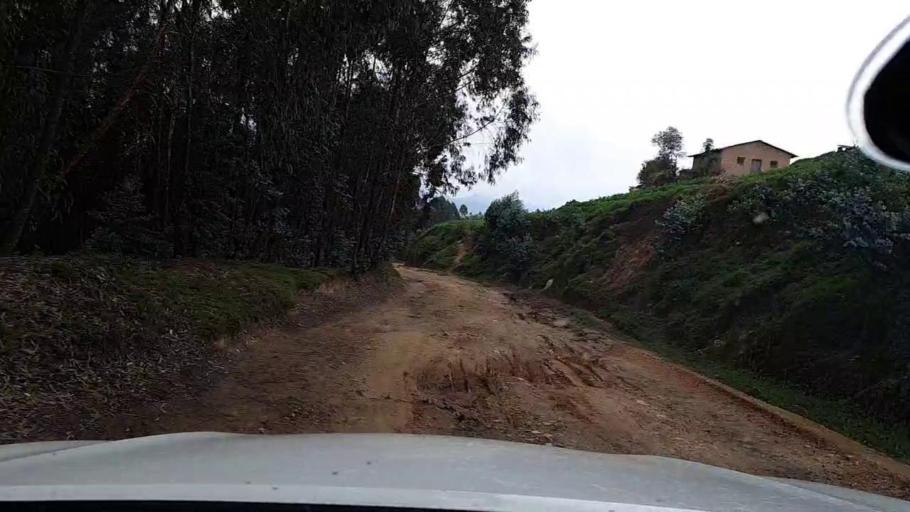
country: RW
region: Western Province
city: Kibuye
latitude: -2.2498
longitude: 29.3457
